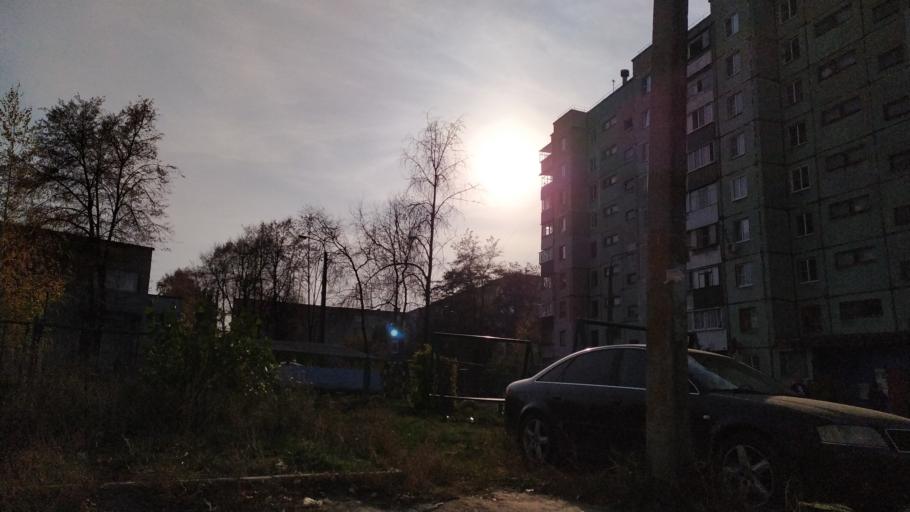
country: RU
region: Kursk
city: Kursk
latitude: 51.6486
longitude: 36.1381
